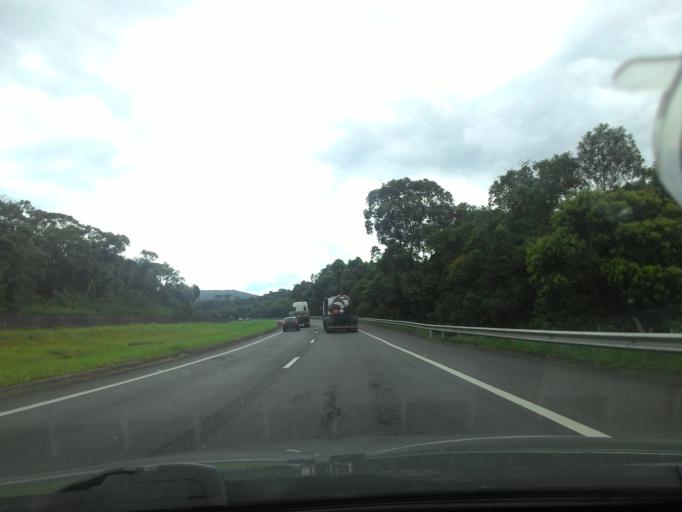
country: BR
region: Sao Paulo
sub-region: Cajati
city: Cajati
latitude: -24.9675
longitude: -48.3870
